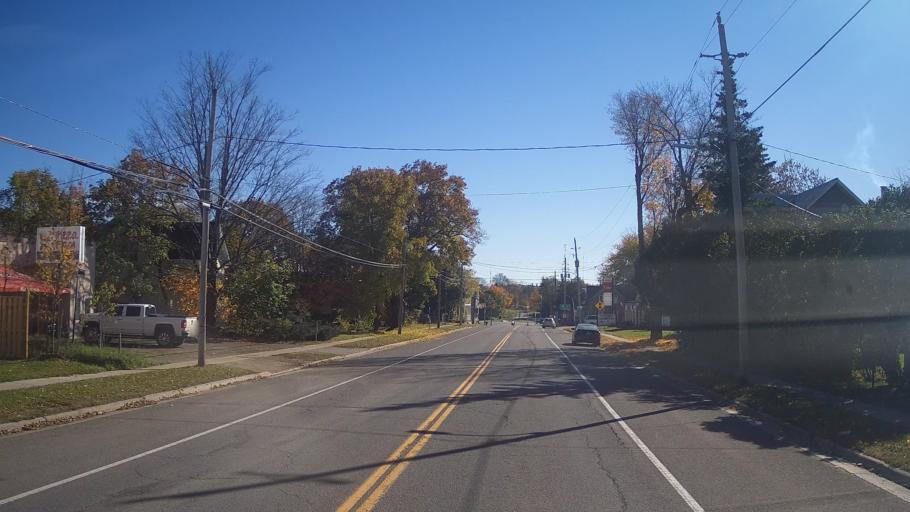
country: CA
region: Ontario
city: Kingston
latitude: 44.4063
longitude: -76.6657
